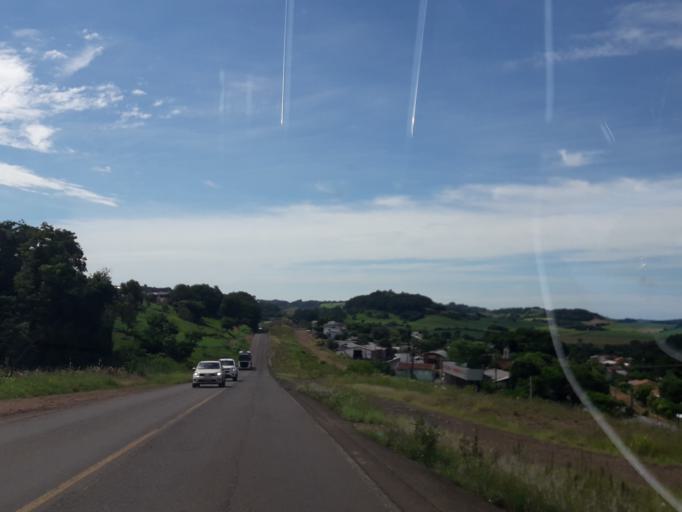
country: AR
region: Misiones
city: Bernardo de Irigoyen
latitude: -26.3789
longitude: -53.5275
